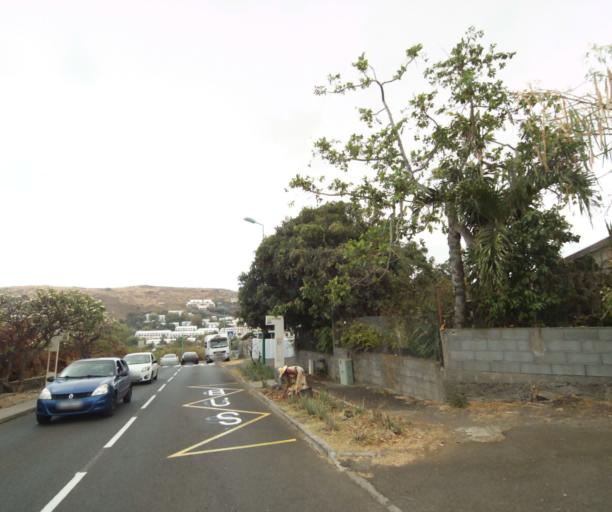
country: RE
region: Reunion
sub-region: Reunion
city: Saint-Paul
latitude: -21.0557
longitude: 55.2282
